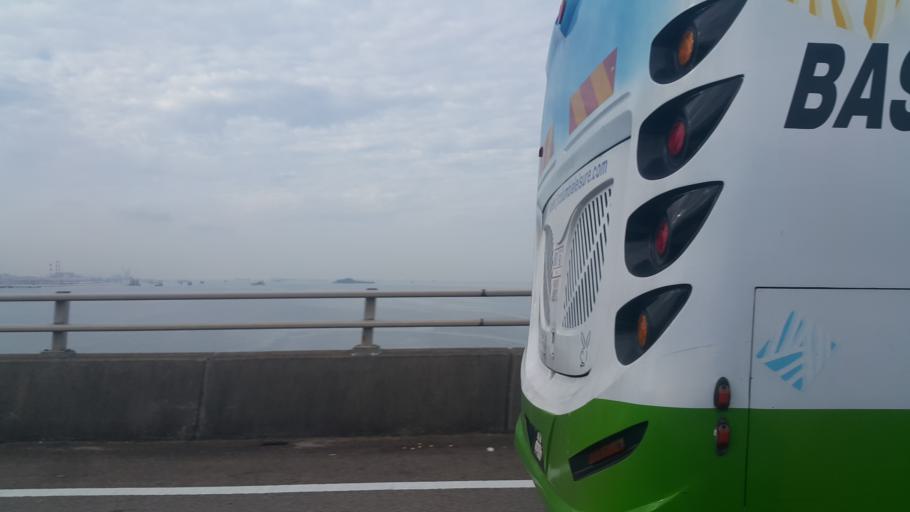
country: MY
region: Johor
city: Johor Bahru
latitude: 1.3521
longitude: 103.6313
